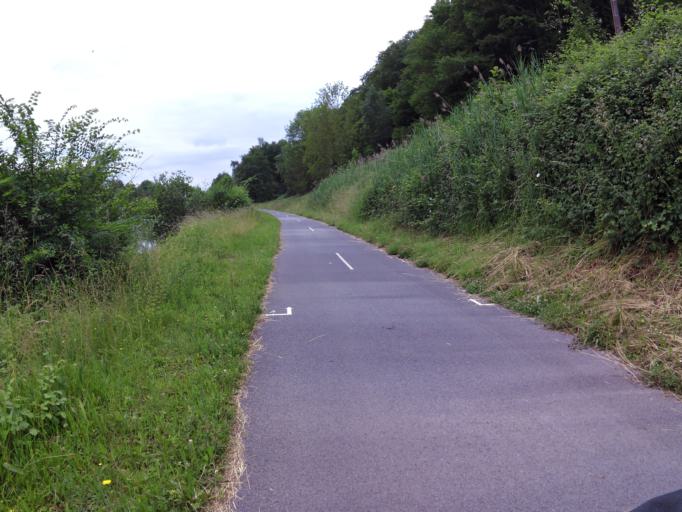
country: FR
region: Champagne-Ardenne
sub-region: Departement des Ardennes
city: Villers-Semeuse
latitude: 49.7553
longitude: 4.7563
